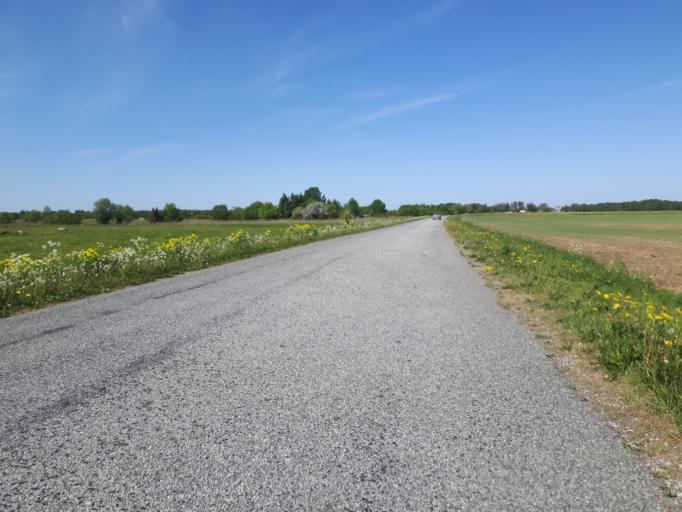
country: EE
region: Ida-Virumaa
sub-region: Aseri vald
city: Aseri
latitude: 59.4713
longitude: 26.8098
